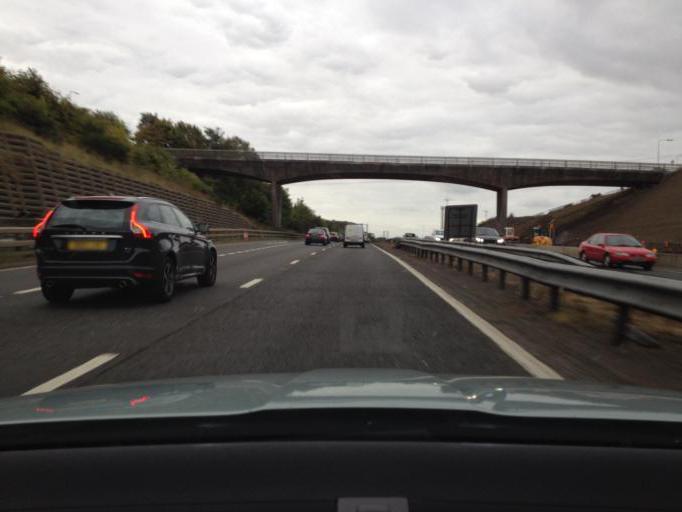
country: GB
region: Scotland
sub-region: Fife
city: Inverkeithing
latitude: 56.0310
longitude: -3.4082
